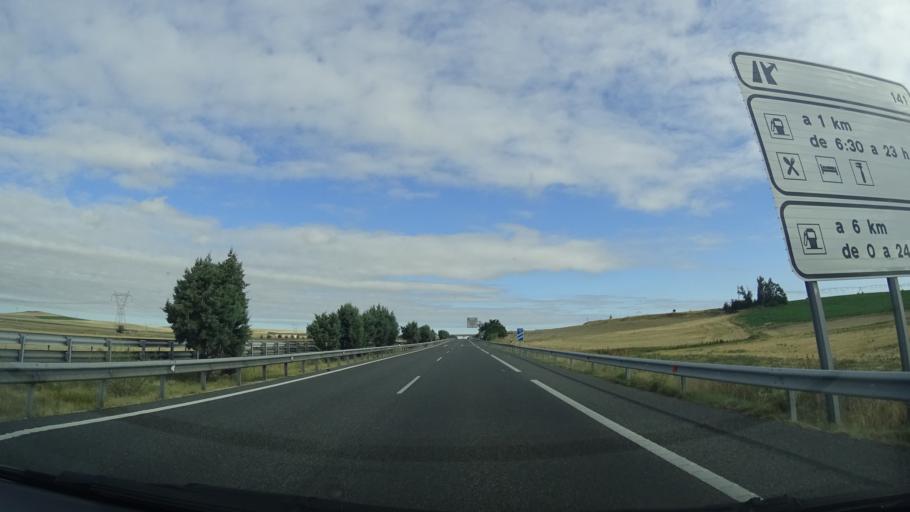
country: ES
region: Castille and Leon
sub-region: Provincia de Valladolid
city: Ataquines
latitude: 41.1714
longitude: -4.8025
